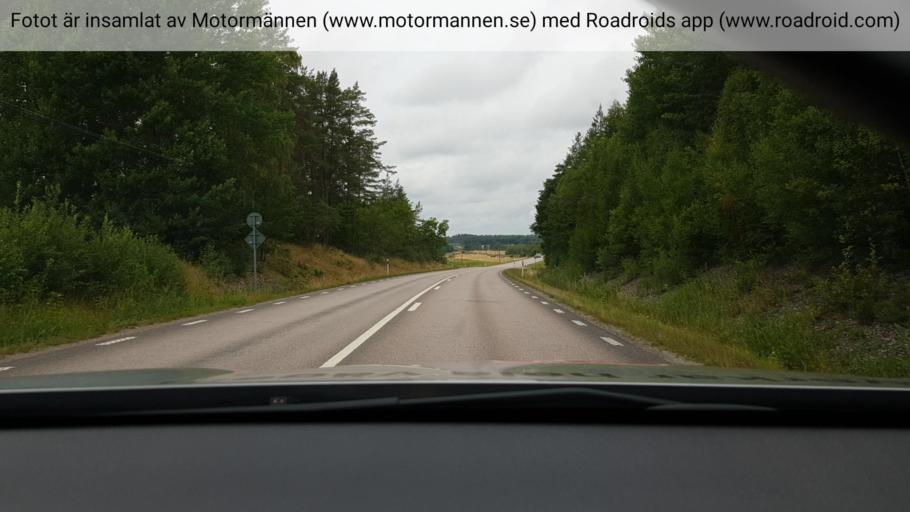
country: SE
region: Soedermanland
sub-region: Gnesta Kommun
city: Gnesta
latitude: 59.0553
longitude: 17.2007
